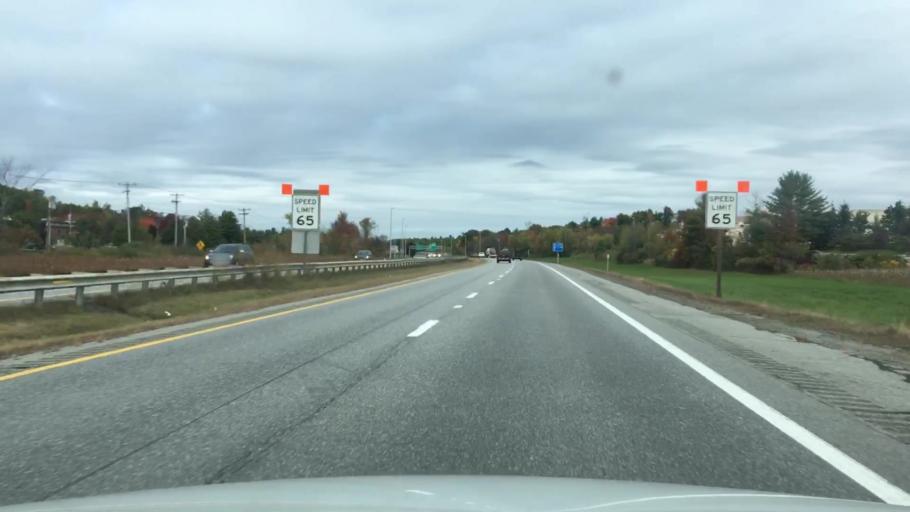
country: US
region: Maine
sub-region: Kennebec County
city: Hallowell
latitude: 44.3062
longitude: -69.8078
